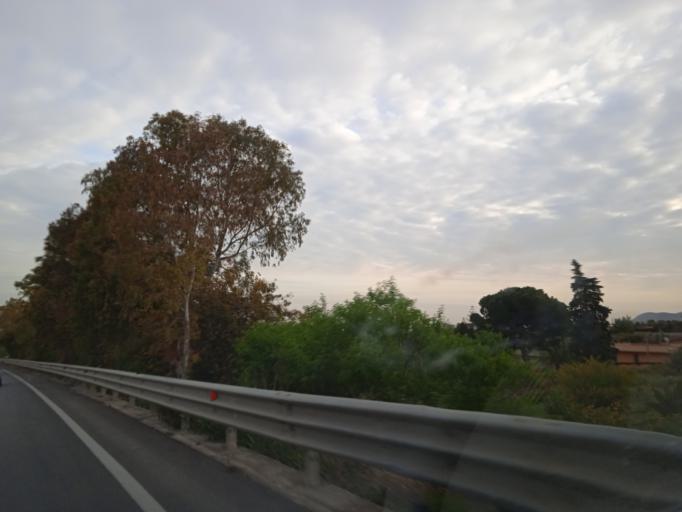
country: IT
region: Sicily
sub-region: Palermo
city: Portella di Mare
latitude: 38.0676
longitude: 13.4603
